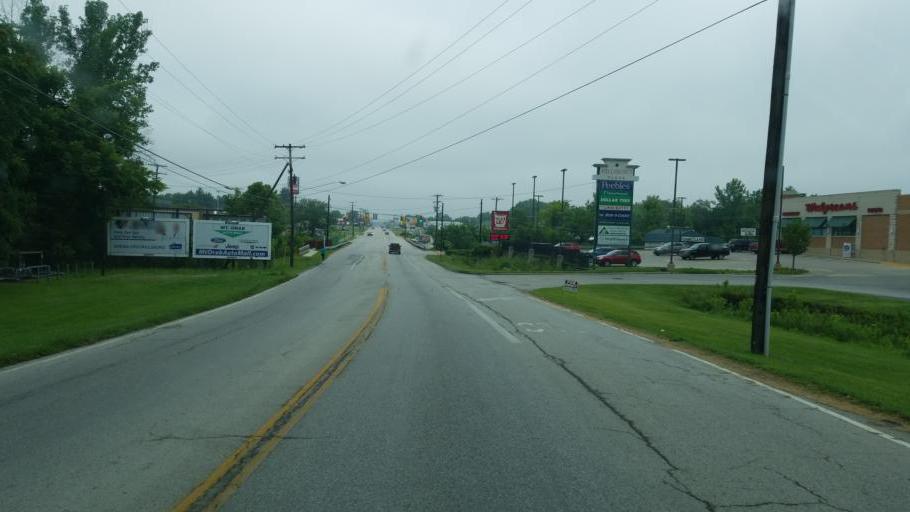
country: US
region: Ohio
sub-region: Highland County
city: Hillsboro
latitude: 39.2185
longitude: -83.6081
